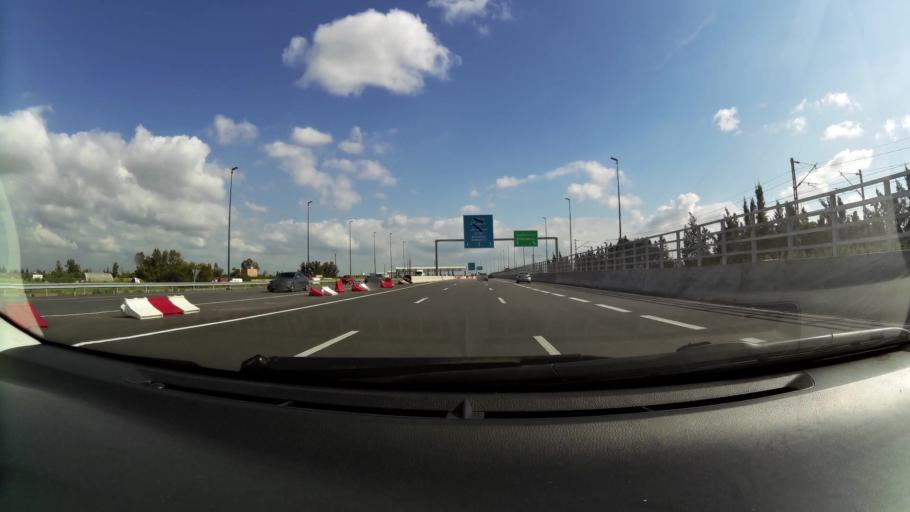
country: MA
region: Chaouia-Ouardigha
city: Nouaseur
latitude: 33.3245
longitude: -7.6063
